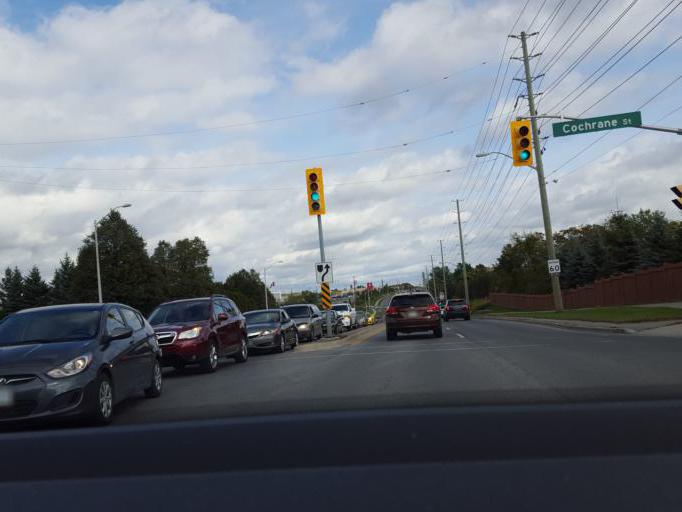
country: CA
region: Ontario
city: Ajax
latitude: 43.9130
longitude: -78.9671
